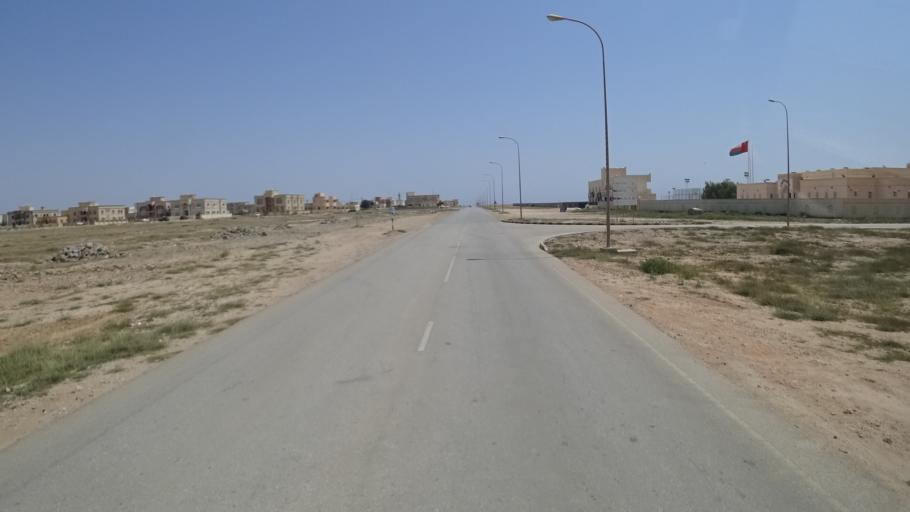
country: OM
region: Zufar
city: Salalah
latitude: 16.9848
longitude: 54.7009
